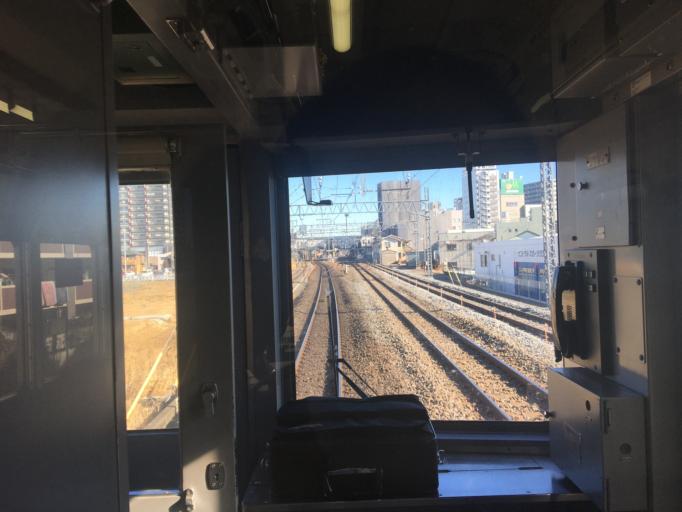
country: JP
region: Saitama
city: Iwatsuki
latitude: 35.9480
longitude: 139.6903
